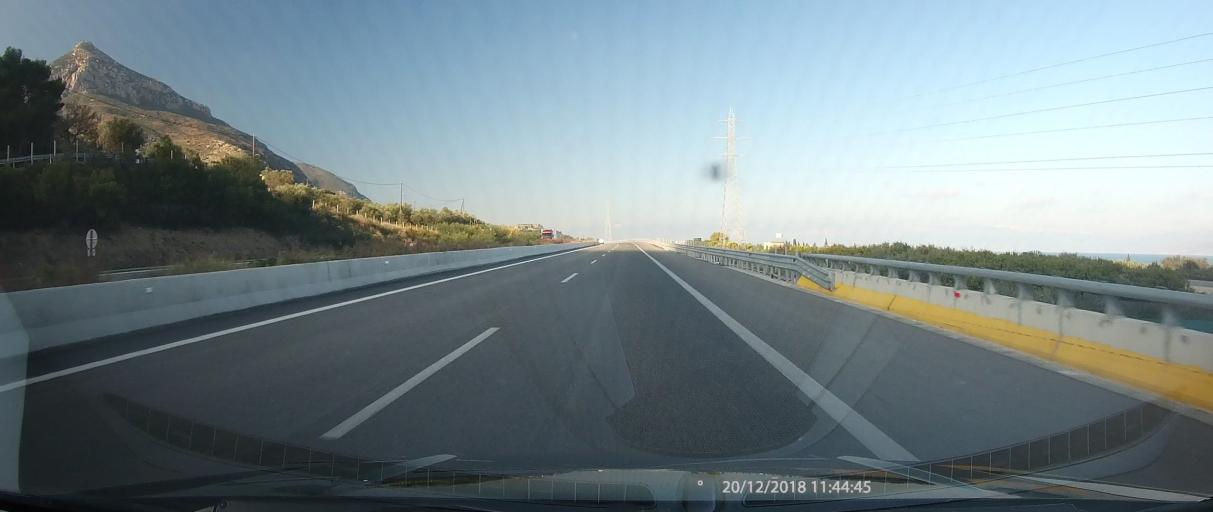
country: GR
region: Peloponnese
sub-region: Nomos Korinthias
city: Xylokastro
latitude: 38.0829
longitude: 22.5912
